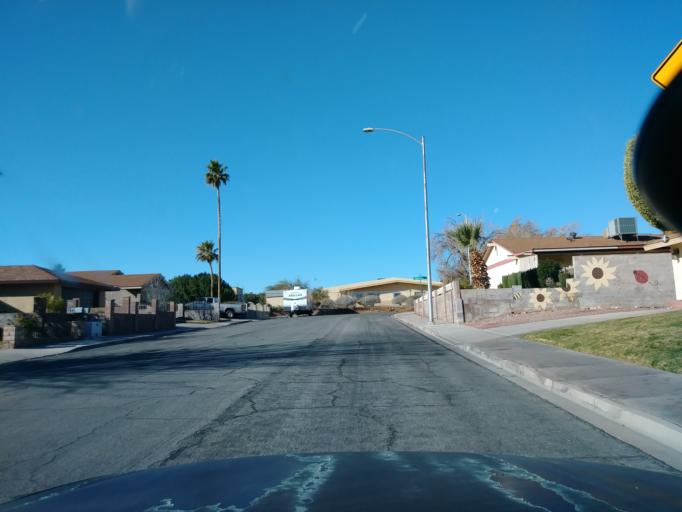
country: US
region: Nevada
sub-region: Clark County
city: Spring Valley
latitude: 36.1508
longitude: -115.2322
